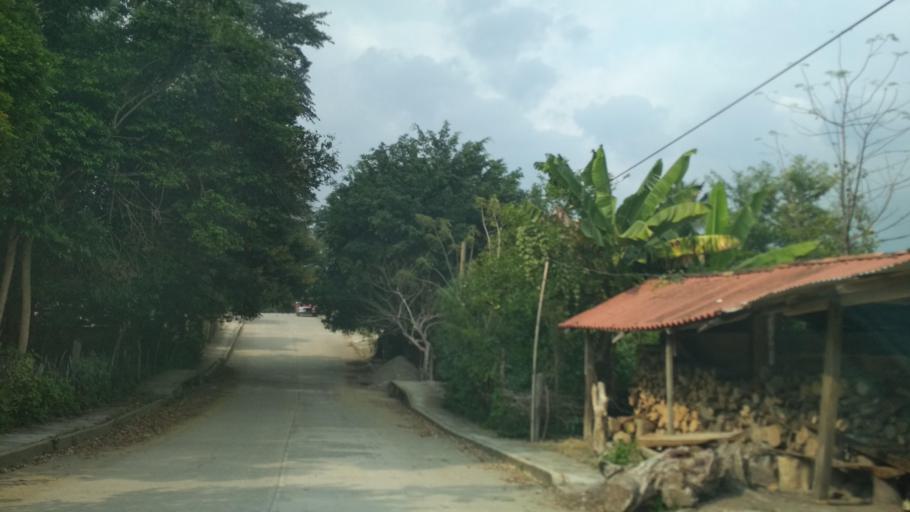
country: MM
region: Kayah
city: Loikaw
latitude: 20.2402
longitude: 97.2758
